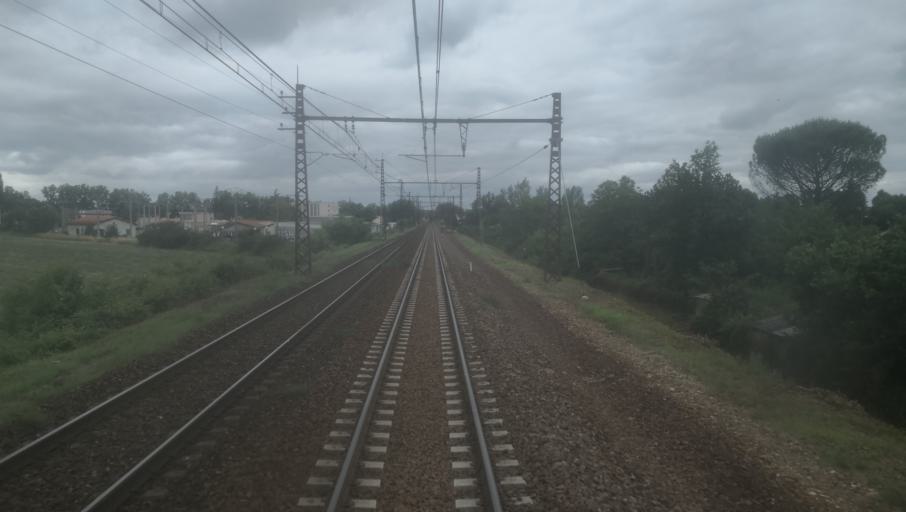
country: FR
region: Midi-Pyrenees
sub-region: Departement du Tarn-et-Garonne
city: Montauban
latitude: 43.9996
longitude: 1.3356
